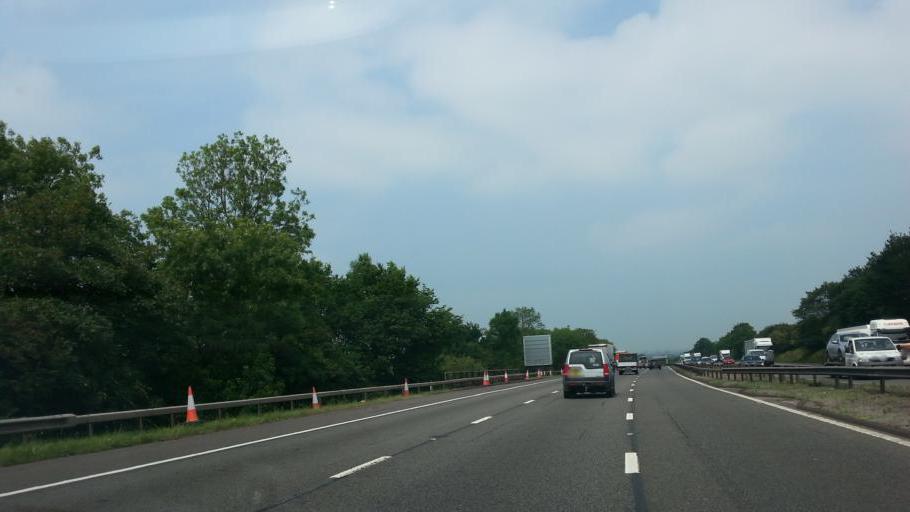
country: GB
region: England
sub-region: Staffordshire
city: Stafford
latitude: 52.8030
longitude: -2.1542
